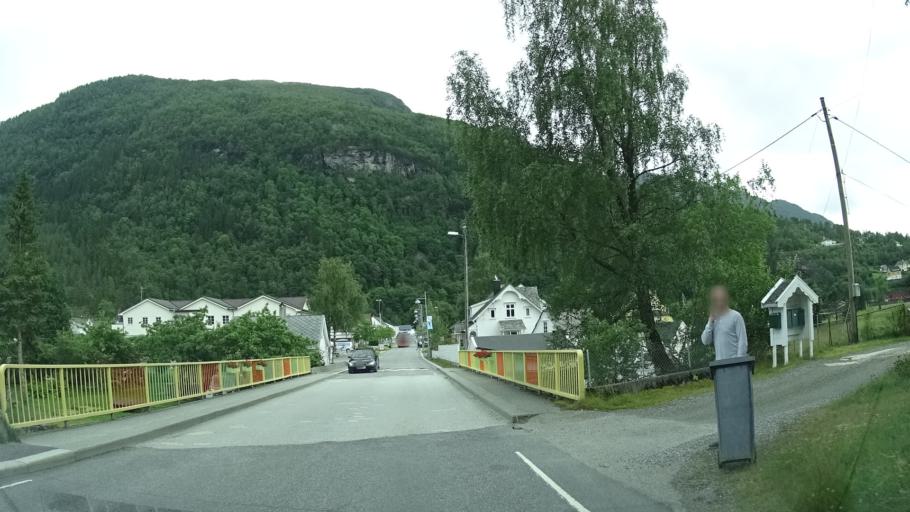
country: NO
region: Hordaland
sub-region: Jondal
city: Jondal
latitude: 60.2778
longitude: 6.2514
